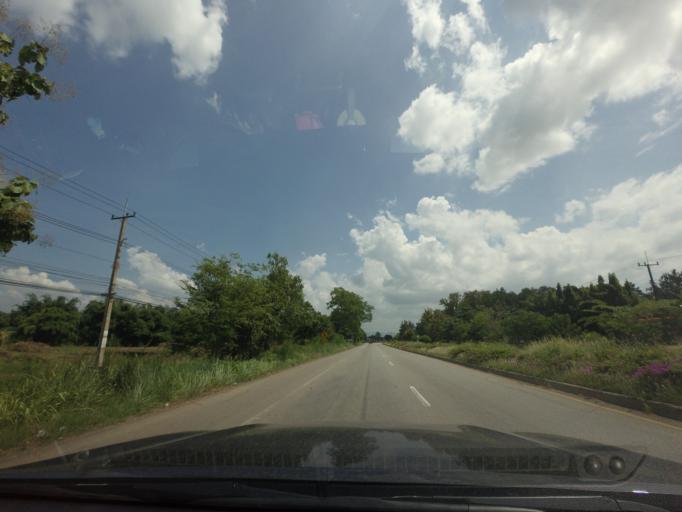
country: TH
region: Phetchabun
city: Phetchabun
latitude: 16.2519
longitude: 101.0659
